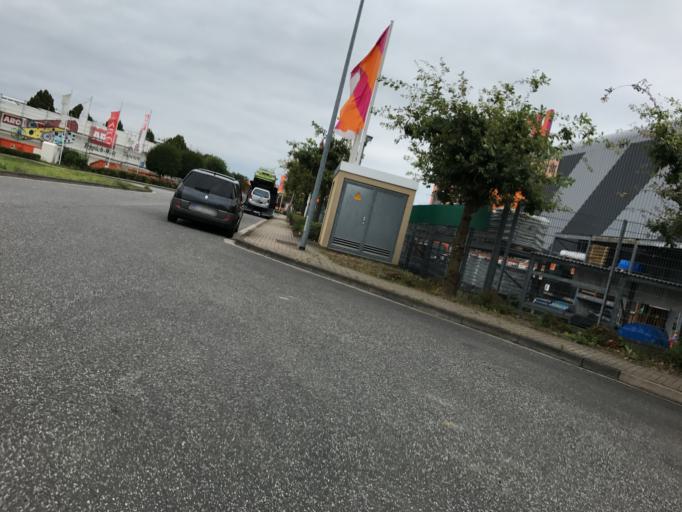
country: DE
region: Rheinland-Pfalz
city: Klein-Winternheim
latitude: 49.9670
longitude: 8.2366
